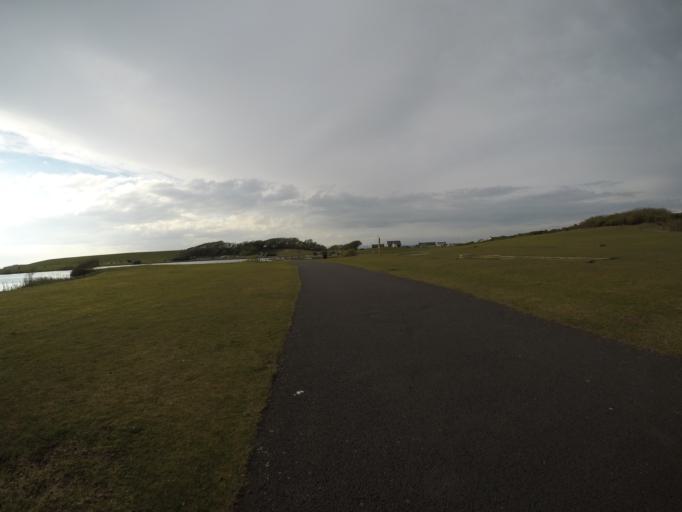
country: GB
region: Scotland
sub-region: North Ayrshire
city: Irvine
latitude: 55.6047
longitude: -4.6861
